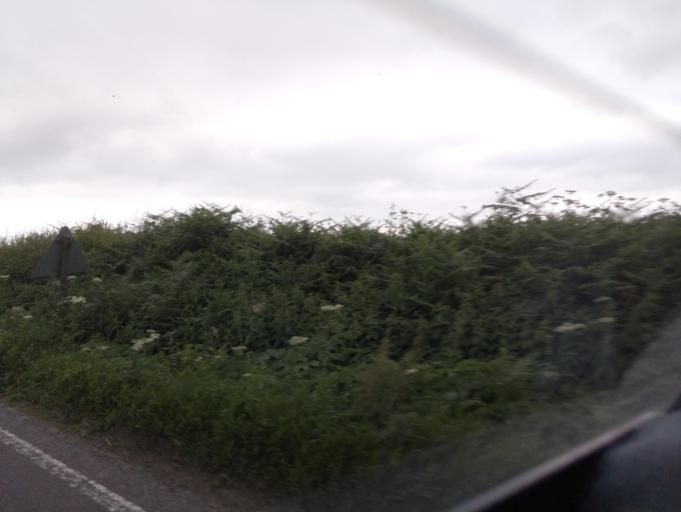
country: GB
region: England
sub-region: Derbyshire
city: Rodsley
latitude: 52.9120
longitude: -1.7611
